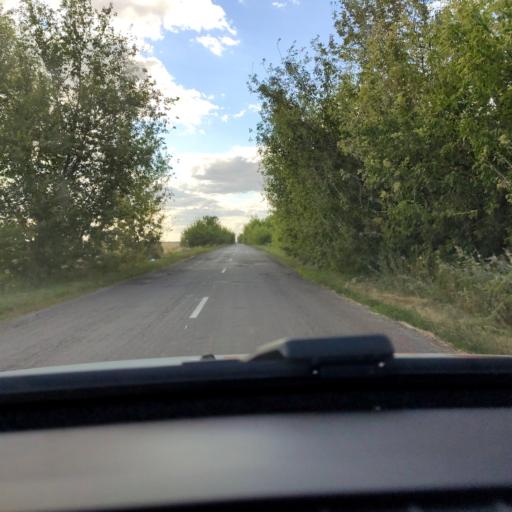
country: RU
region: Voronezj
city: Orlovo
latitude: 51.6281
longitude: 39.7760
